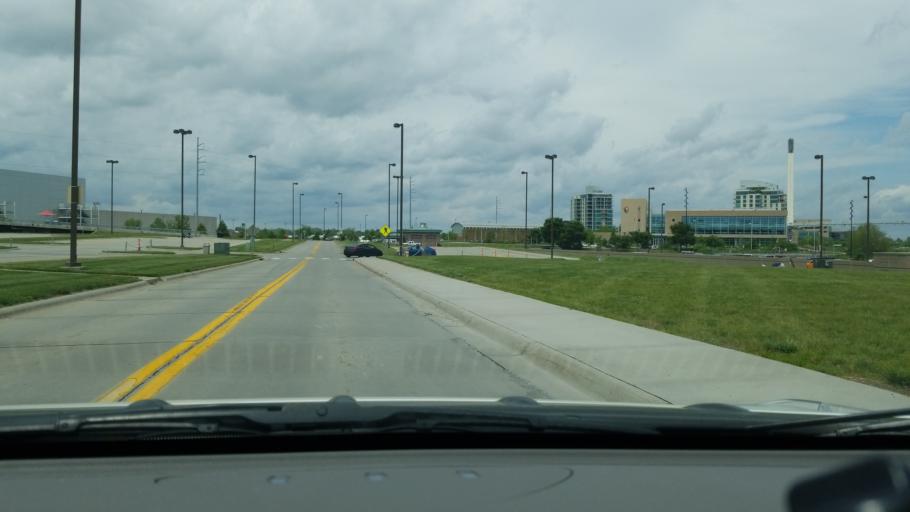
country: US
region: Nebraska
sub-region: Douglas County
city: Omaha
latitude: 41.2619
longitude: -95.9245
